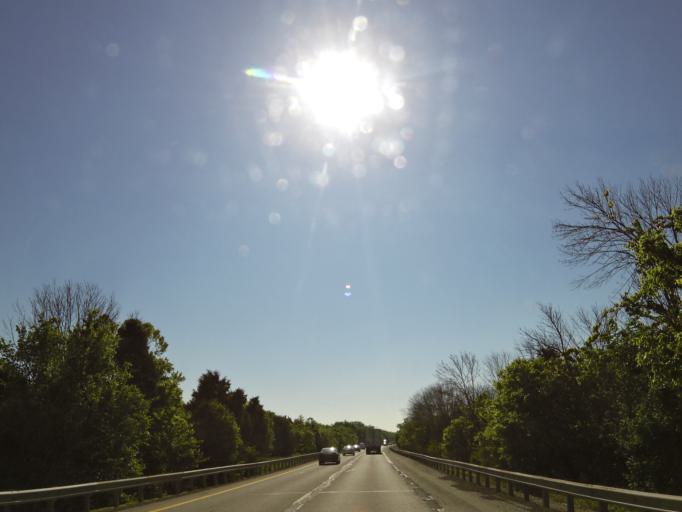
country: US
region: Kentucky
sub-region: Franklin County
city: Frankfort
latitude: 38.1501
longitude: -85.0484
